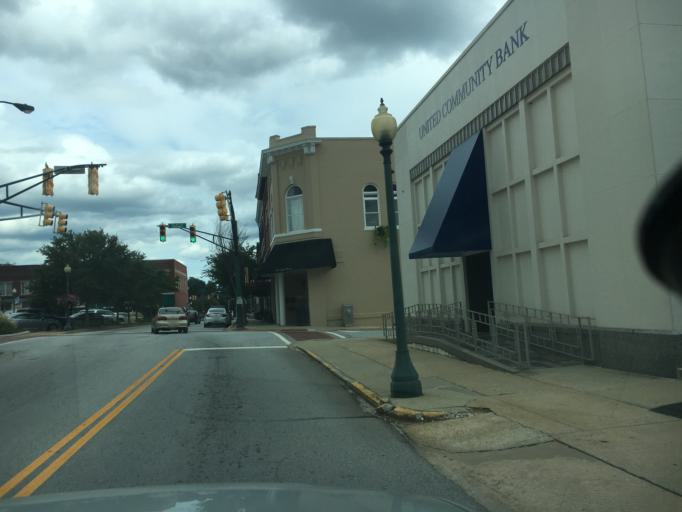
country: US
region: South Carolina
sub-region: Laurens County
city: Laurens
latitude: 34.4987
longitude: -82.0152
